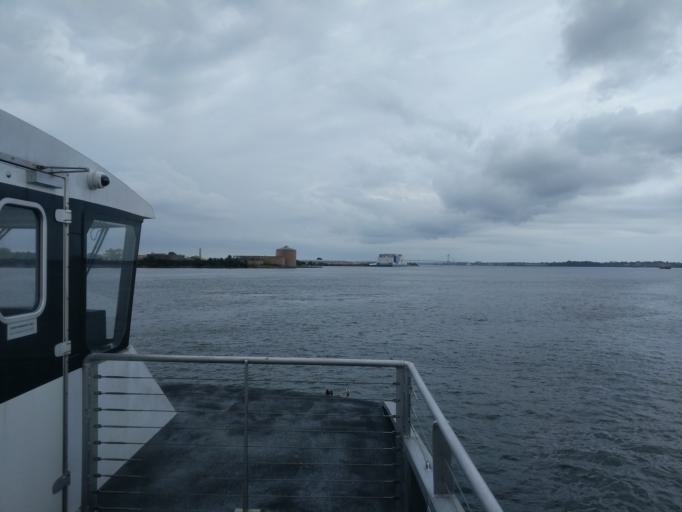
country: US
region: New York
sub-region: Bronx
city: The Bronx
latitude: 40.8004
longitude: -73.8930
